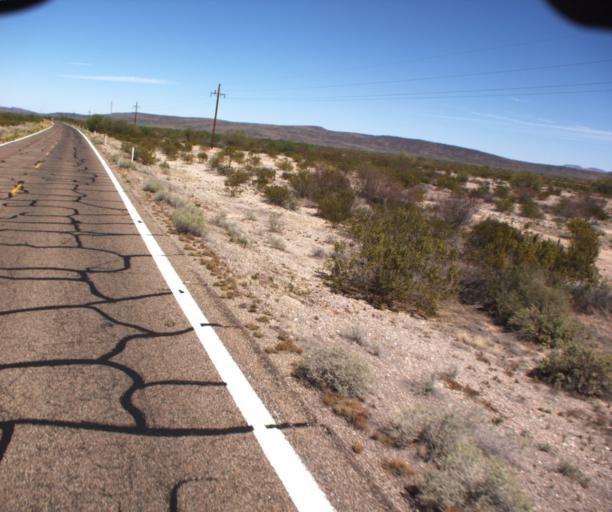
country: US
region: Arizona
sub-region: Pima County
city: Ajo
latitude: 32.4451
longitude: -112.8710
